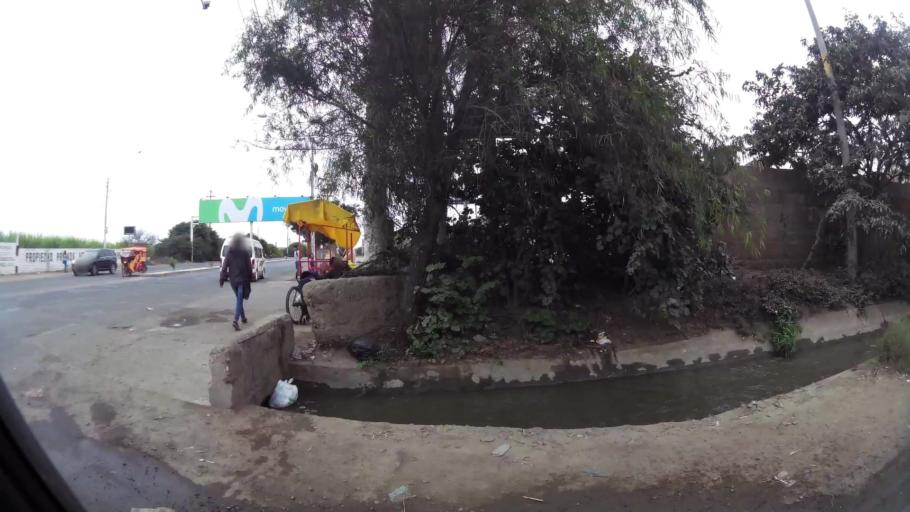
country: PE
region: La Libertad
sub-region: Provincia de Trujillo
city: La Esperanza
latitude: -8.1009
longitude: -79.0572
